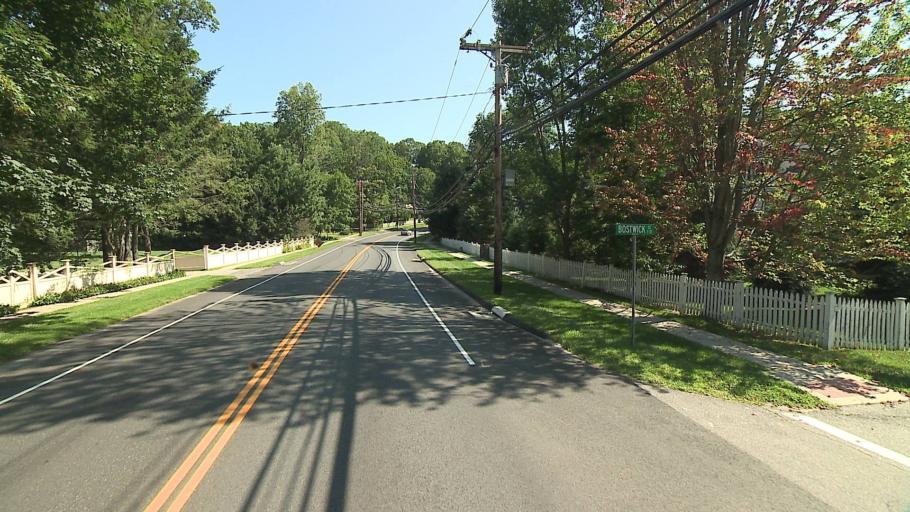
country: US
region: Connecticut
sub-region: Litchfield County
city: Canaan
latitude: 41.9679
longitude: -73.4387
